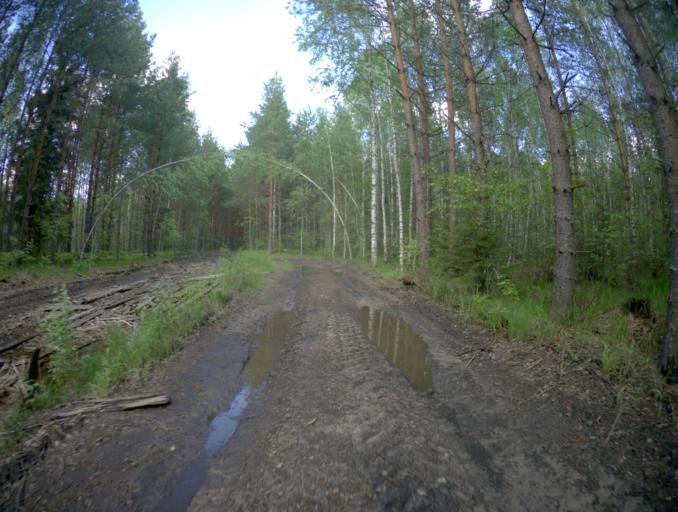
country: RU
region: Vladimir
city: Zolotkovo
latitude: 55.3225
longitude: 40.9340
